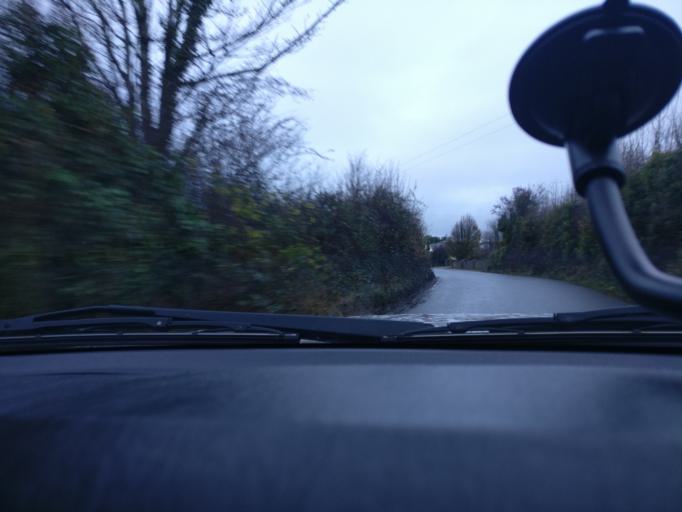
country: IE
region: Connaught
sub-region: County Galway
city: Loughrea
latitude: 53.2508
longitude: -8.5802
